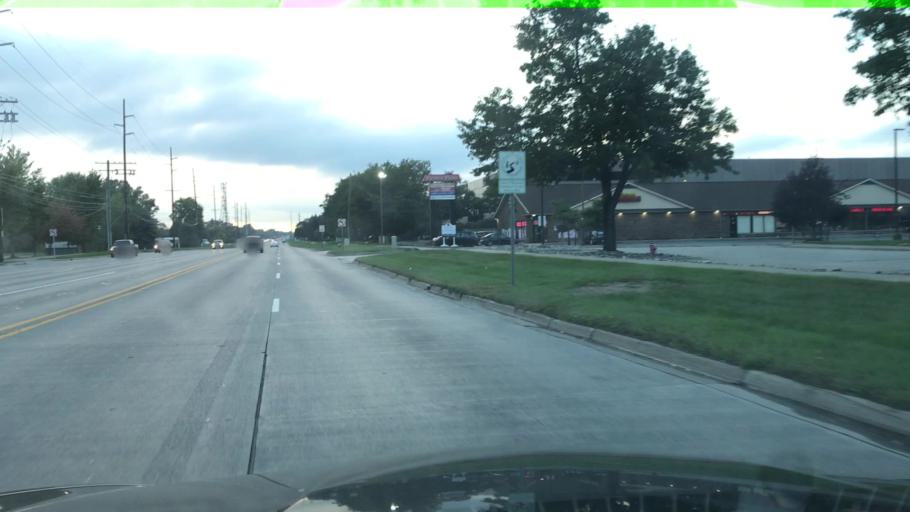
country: US
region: Michigan
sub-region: Macomb County
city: Shelby
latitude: 42.6703
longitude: -82.9950
